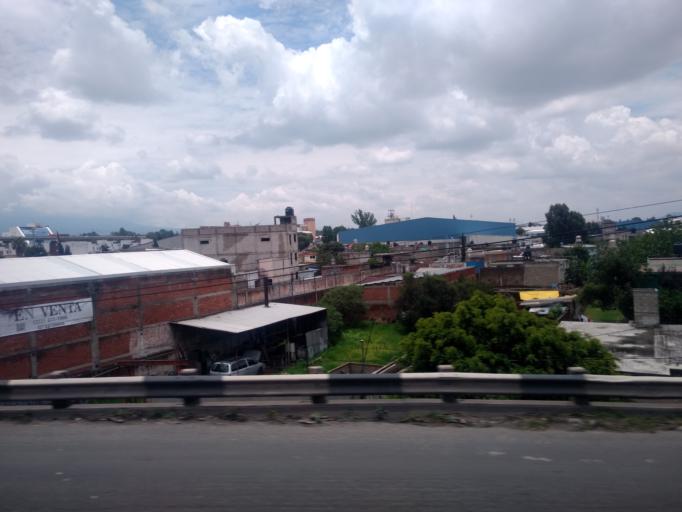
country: MX
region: Puebla
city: Puebla
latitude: 19.0818
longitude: -98.2047
